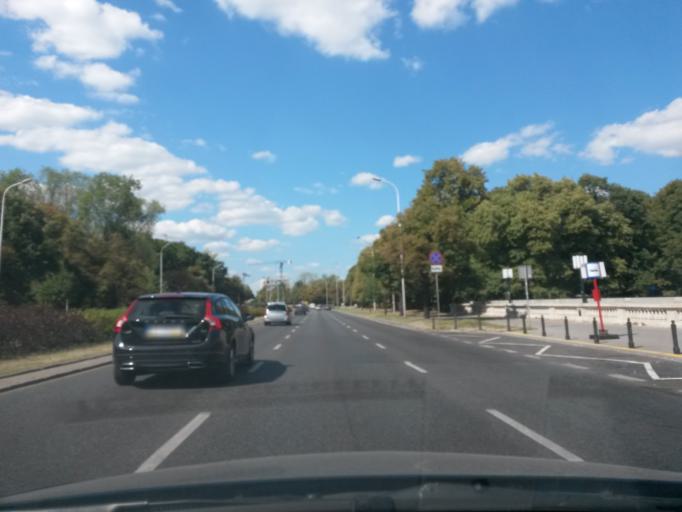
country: PL
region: Masovian Voivodeship
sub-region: Warszawa
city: Srodmiescie
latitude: 52.2287
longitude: 21.0423
